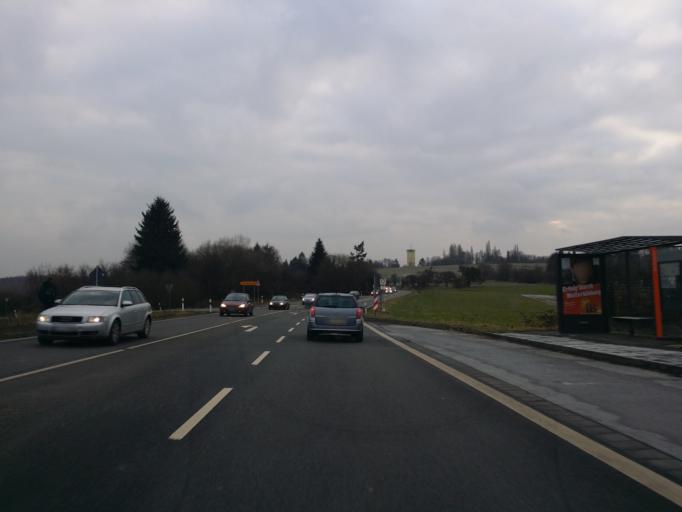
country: DE
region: Hesse
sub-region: Regierungsbezirk Darmstadt
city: Wiesbaden
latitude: 50.1101
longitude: 8.2816
